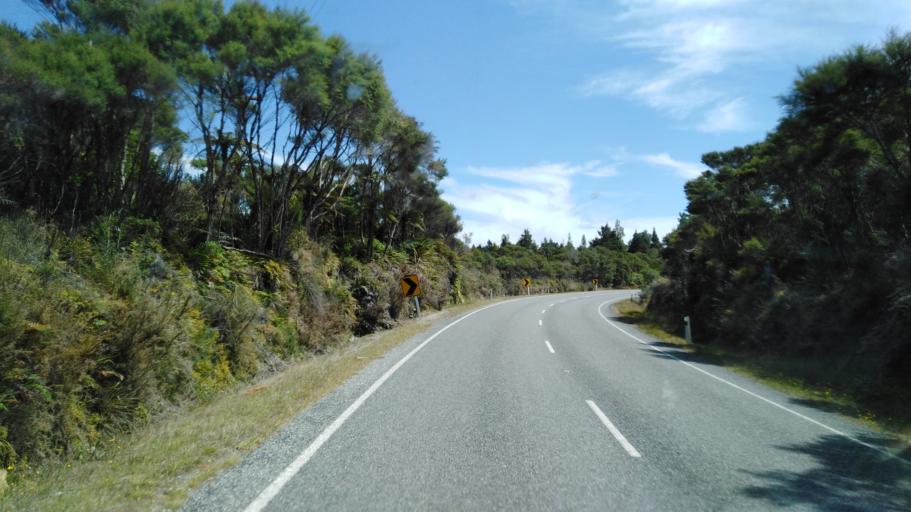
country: NZ
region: West Coast
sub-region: Buller District
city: Westport
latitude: -41.7462
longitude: 171.7215
